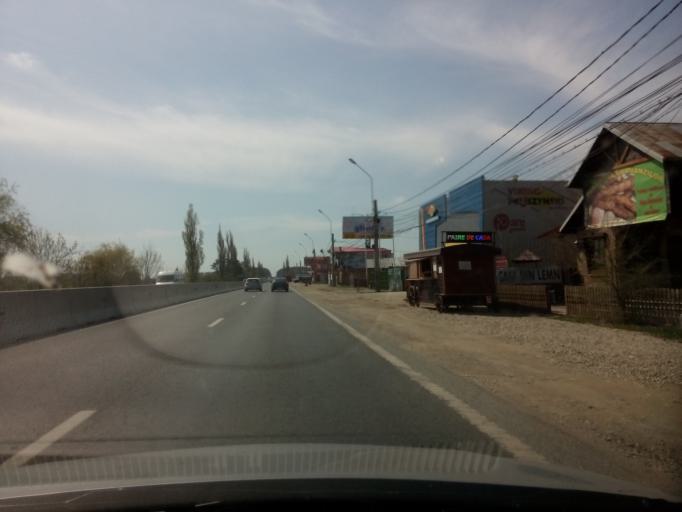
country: RO
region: Ilfov
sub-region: Comuna Corbeanca
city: Corbeanca
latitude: 44.5994
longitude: 26.0714
